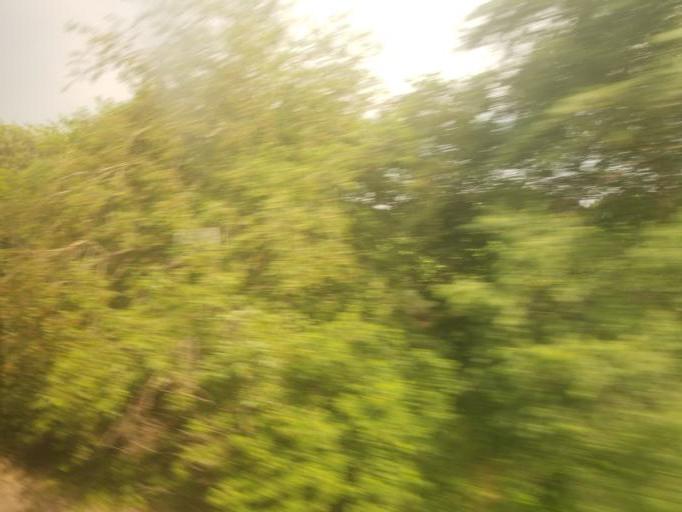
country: US
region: Illinois
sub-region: Bureau County
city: Princeton
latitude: 41.3428
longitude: -89.6417
